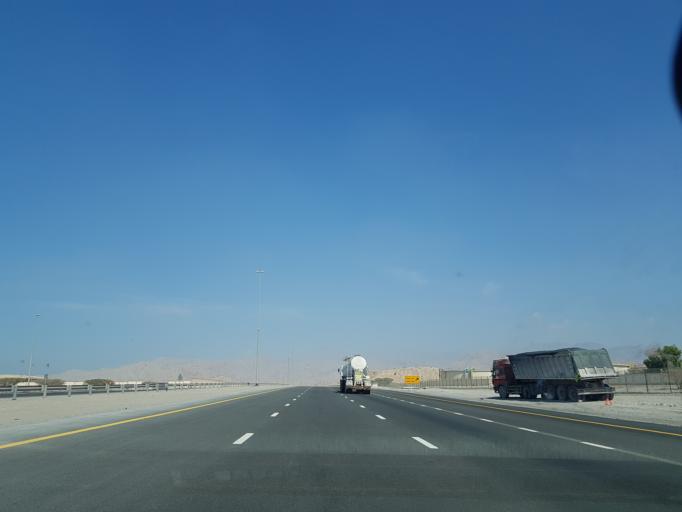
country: AE
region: Ra's al Khaymah
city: Ras al-Khaimah
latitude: 25.7707
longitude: 56.0272
